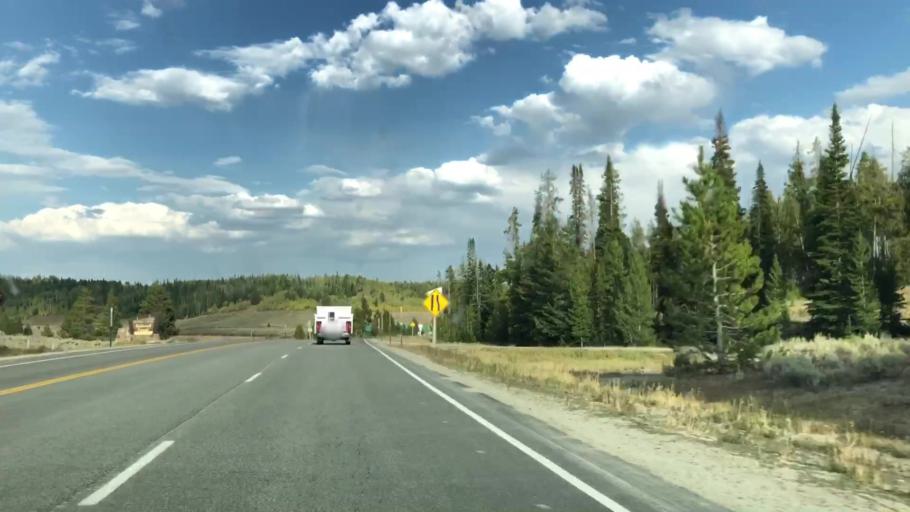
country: US
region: Wyoming
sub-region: Sublette County
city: Pinedale
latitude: 43.1325
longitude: -110.2013
